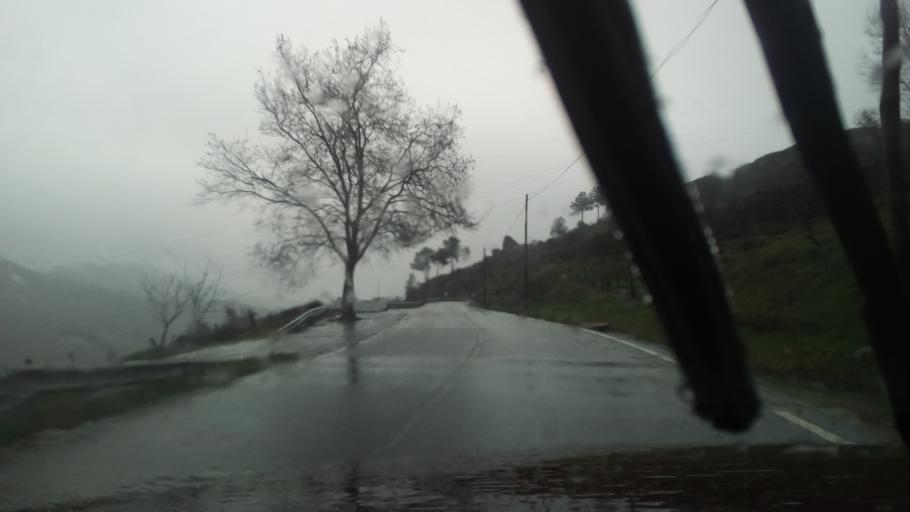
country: PT
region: Guarda
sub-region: Guarda
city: Guarda
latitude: 40.5442
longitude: -7.3241
